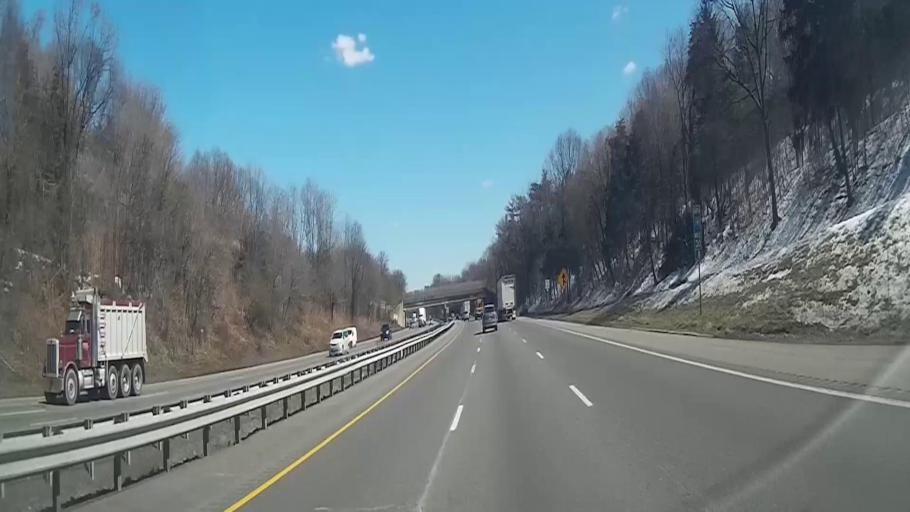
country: US
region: New Jersey
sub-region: Camden County
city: Lawnside
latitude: 39.8718
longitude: -75.0358
